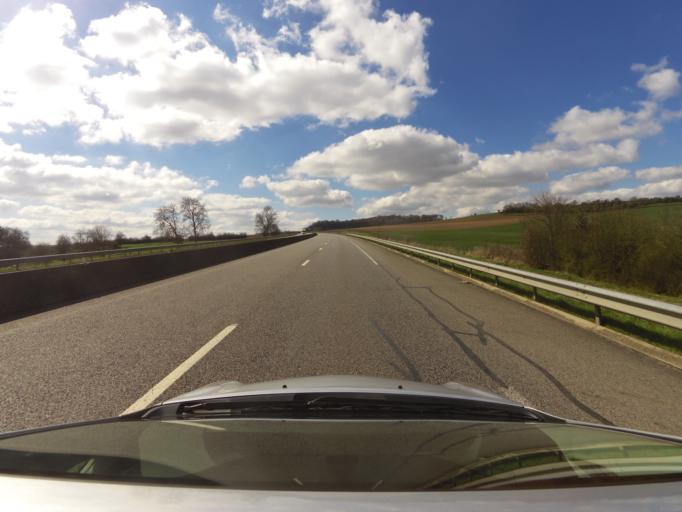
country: FR
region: Haute-Normandie
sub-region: Departement de la Seine-Maritime
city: Foucarmont
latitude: 49.8713
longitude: 1.5610
